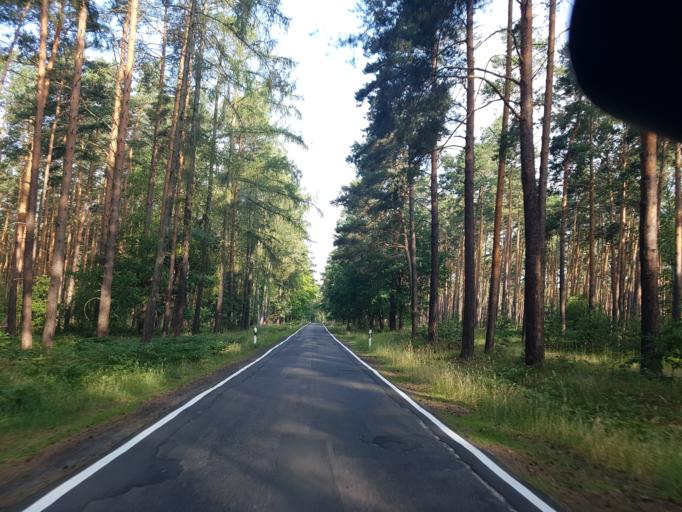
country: DE
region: Saxony-Anhalt
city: Holzdorf
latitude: 51.8559
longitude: 13.0733
